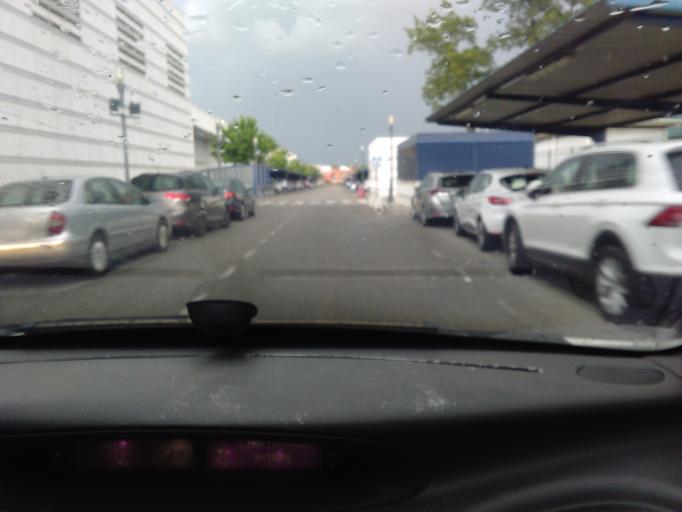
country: ES
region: Andalusia
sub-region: Provincia de Sevilla
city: Sevilla
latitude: 37.3880
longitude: -5.9391
